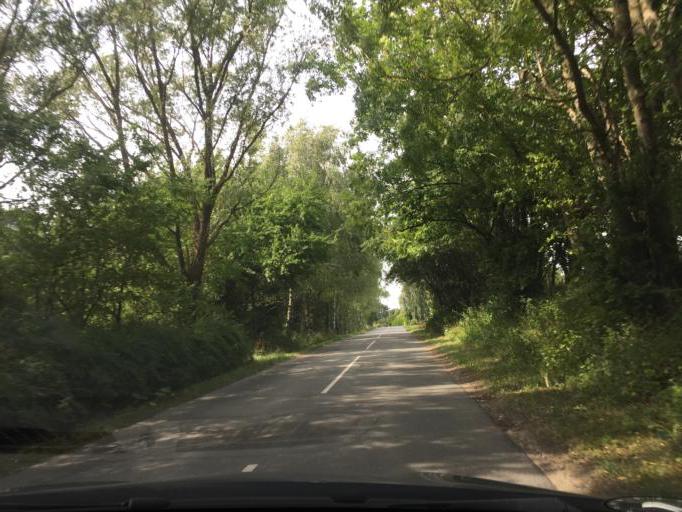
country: DK
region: South Denmark
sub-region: Assens Kommune
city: Vissenbjerg
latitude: 55.3955
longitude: 10.1688
